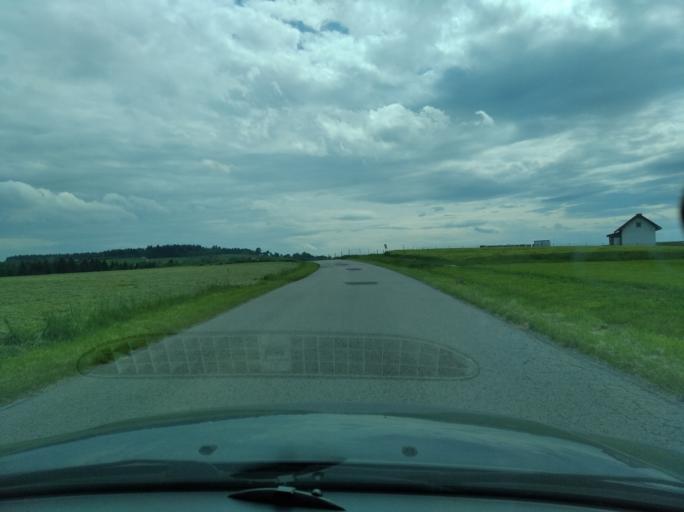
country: PL
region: Subcarpathian Voivodeship
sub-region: Powiat ropczycko-sedziszowski
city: Wielopole Skrzynskie
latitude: 49.9973
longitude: 21.6128
